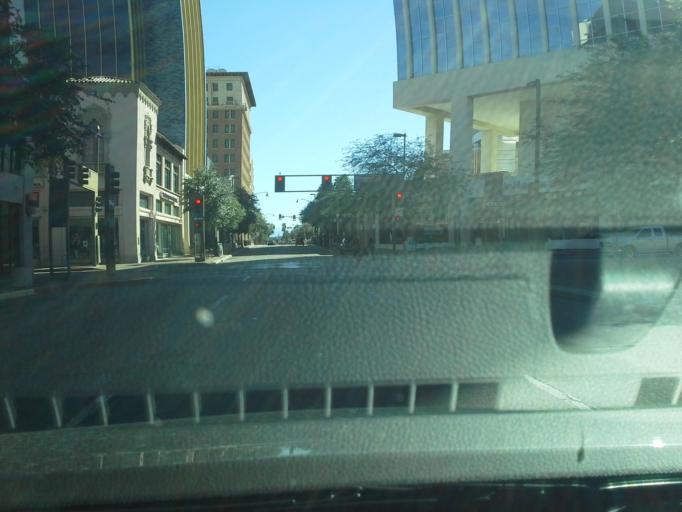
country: US
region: Arizona
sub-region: Pima County
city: South Tucson
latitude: 32.2231
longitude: -110.9714
